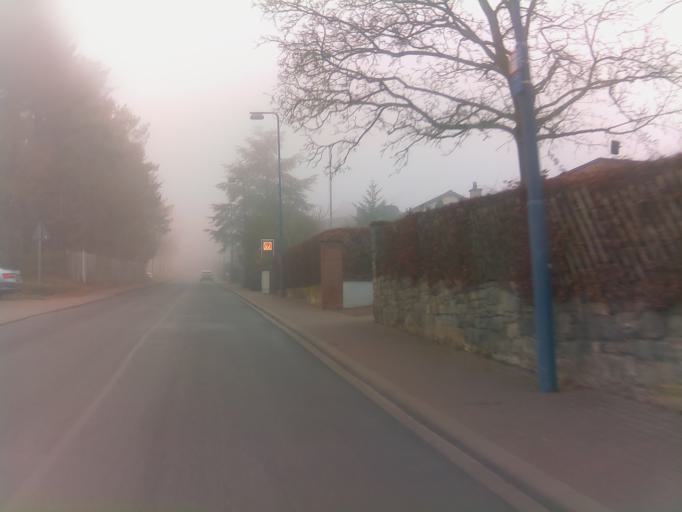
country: DE
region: Rheinland-Pfalz
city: Eisenberg
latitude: 49.5590
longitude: 8.0652
